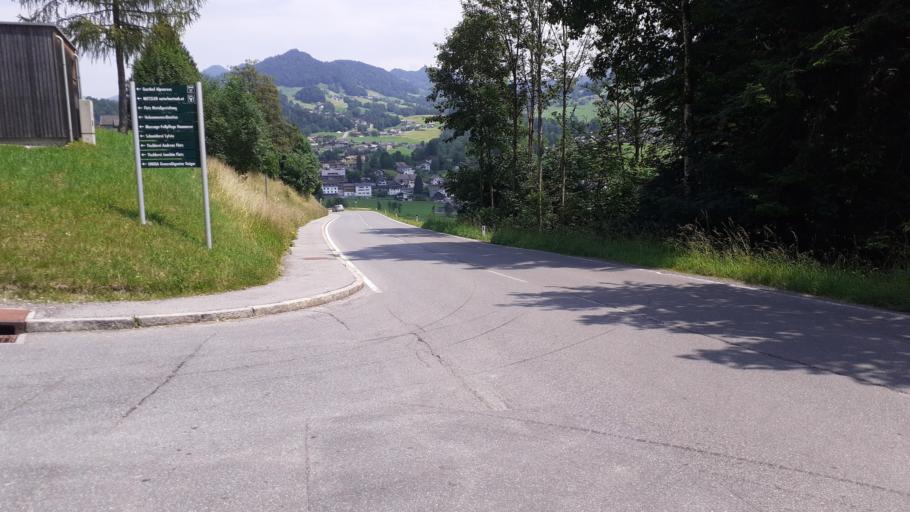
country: AT
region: Vorarlberg
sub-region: Politischer Bezirk Bregenz
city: Egg
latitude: 47.4300
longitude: 9.8873
